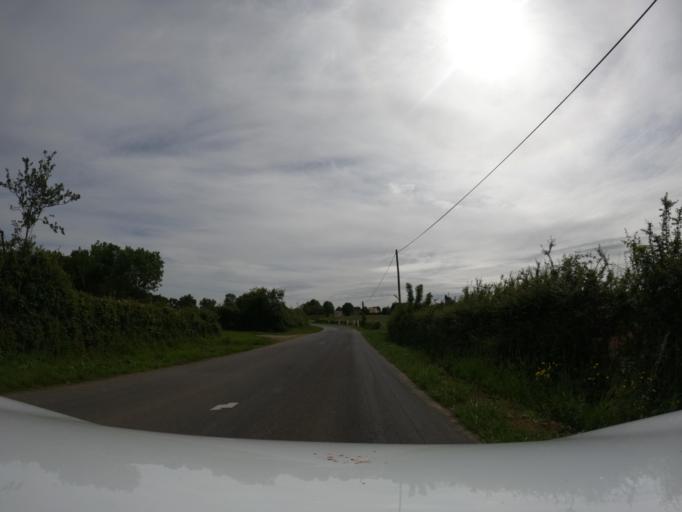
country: FR
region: Pays de la Loire
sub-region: Departement de la Vendee
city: Saint-Hilaire-des-Loges
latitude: 46.5018
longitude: -0.6501
